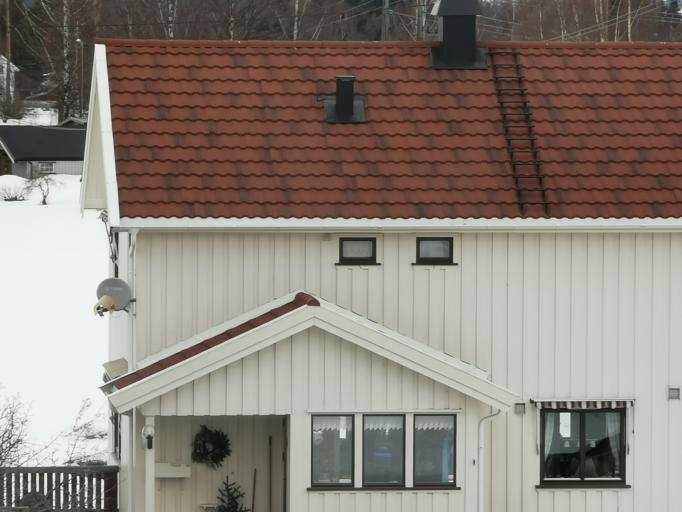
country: NO
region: Hedmark
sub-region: Ringsaker
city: Moelv
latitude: 60.9485
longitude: 10.6133
